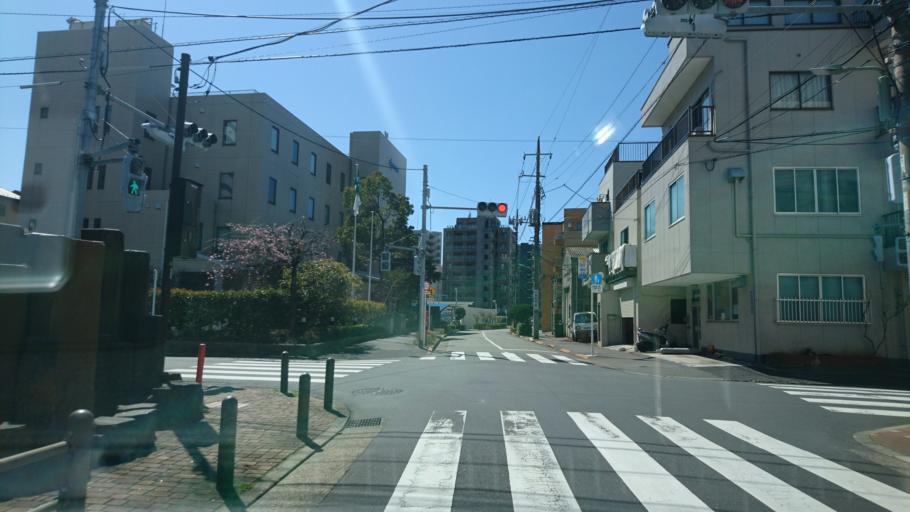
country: JP
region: Kanagawa
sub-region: Kawasaki-shi
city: Kawasaki
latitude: 35.5451
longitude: 139.7203
